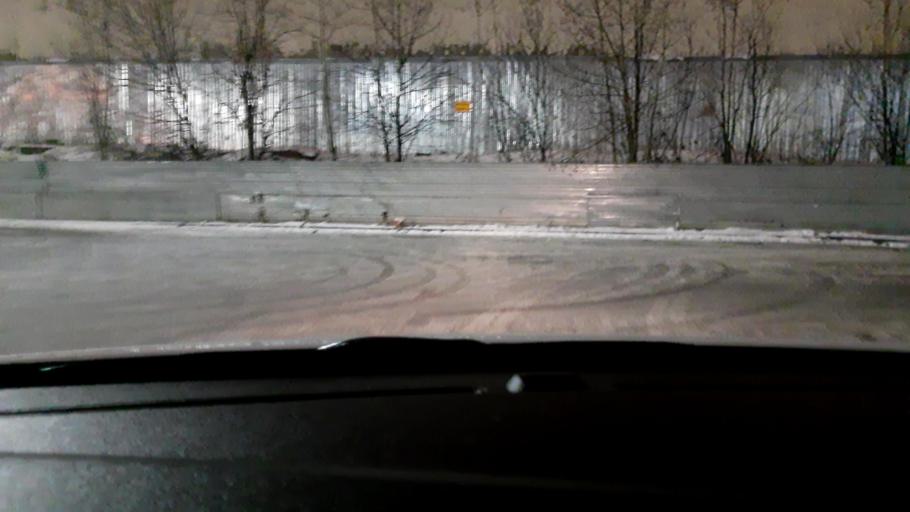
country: RU
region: Moscow
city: Rublevo
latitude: 55.7906
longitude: 37.3875
